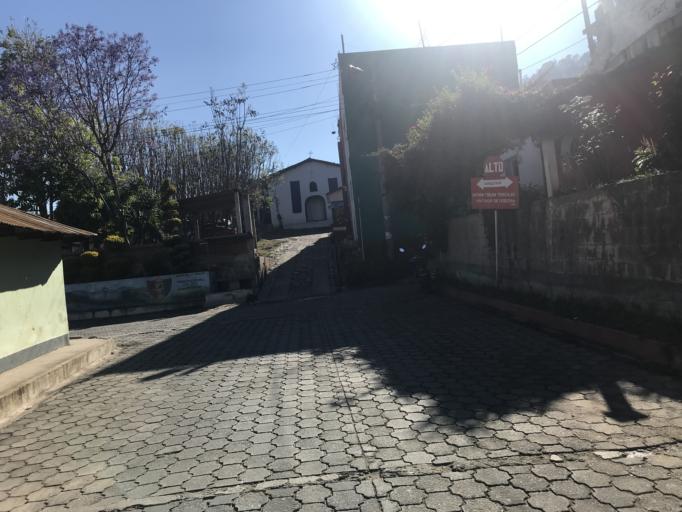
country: GT
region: San Marcos
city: San Miguel Ixtahuacan
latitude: 15.2723
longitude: -91.7456
